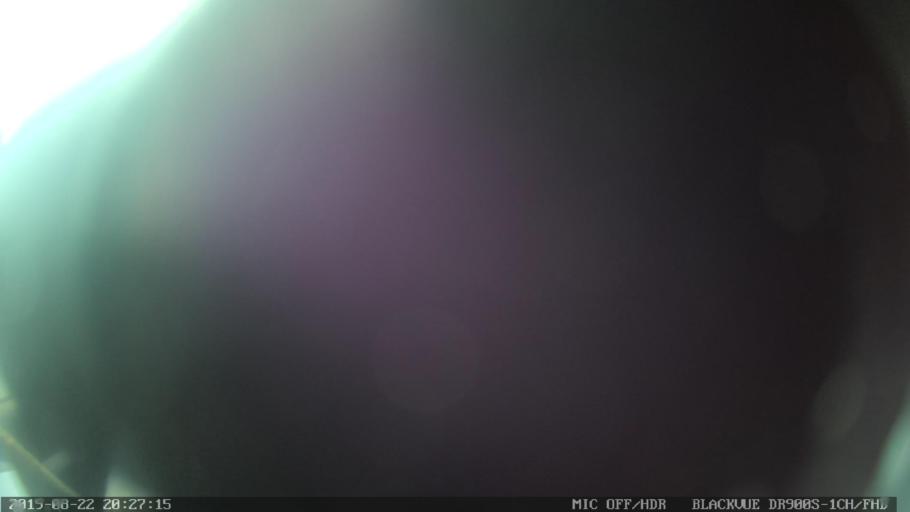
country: PT
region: Castelo Branco
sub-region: Castelo Branco
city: Castelo Branco
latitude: 39.7925
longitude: -7.5638
